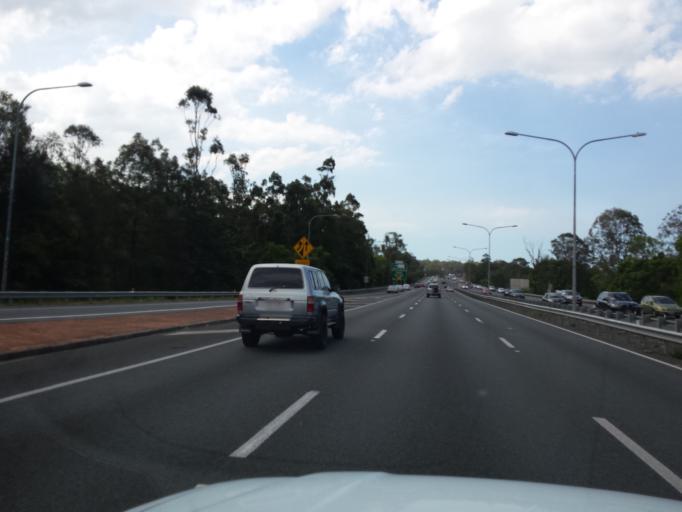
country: AU
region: Queensland
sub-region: Gold Coast
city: Nerang
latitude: -27.9908
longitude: 153.3404
